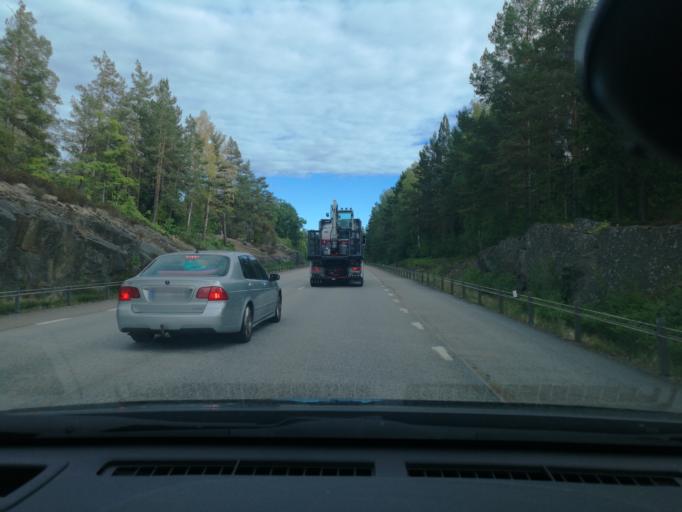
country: SE
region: Kalmar
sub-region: Vasterviks Kommun
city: Ankarsrum
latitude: 57.5317
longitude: 16.4857
